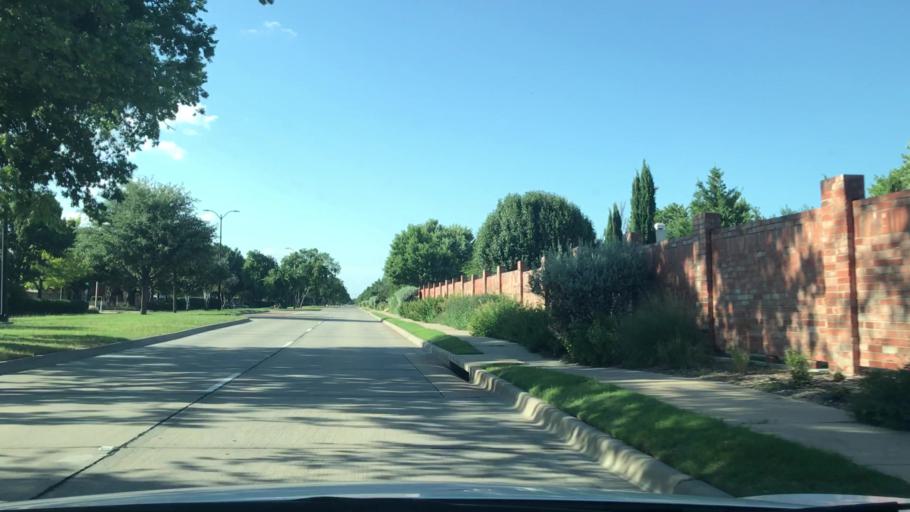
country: US
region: Texas
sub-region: Collin County
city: Frisco
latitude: 33.1172
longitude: -96.7880
